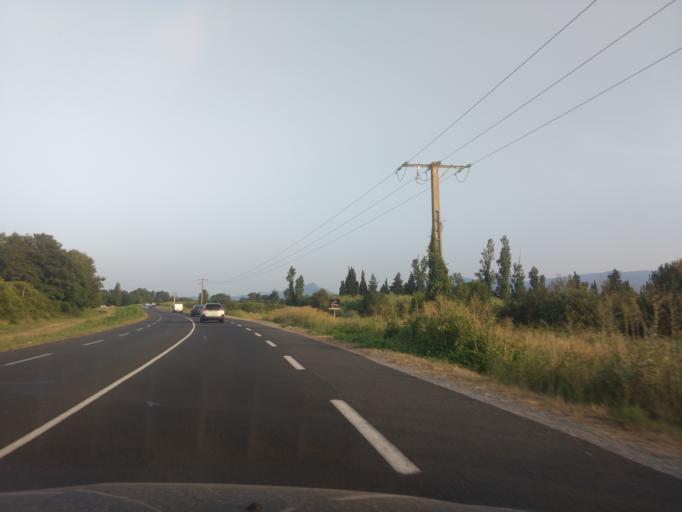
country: FR
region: Languedoc-Roussillon
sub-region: Departement des Pyrenees-Orientales
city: Latour-Bas-Elne
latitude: 42.5908
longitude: 3.0261
